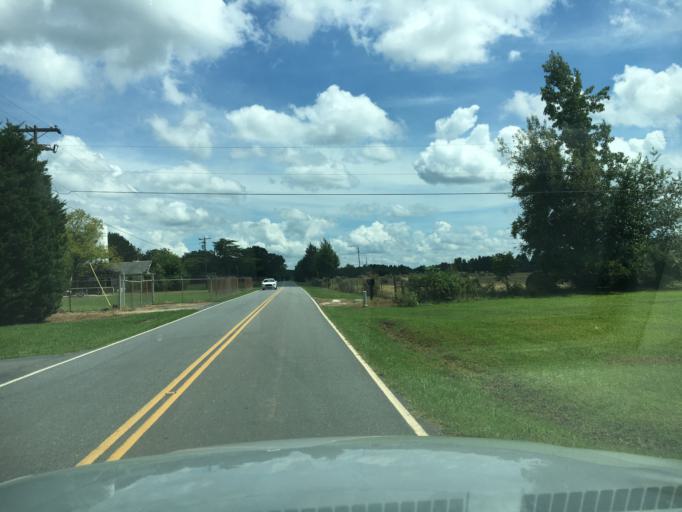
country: US
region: South Carolina
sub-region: Anderson County
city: Belton
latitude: 34.5468
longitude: -82.4570
